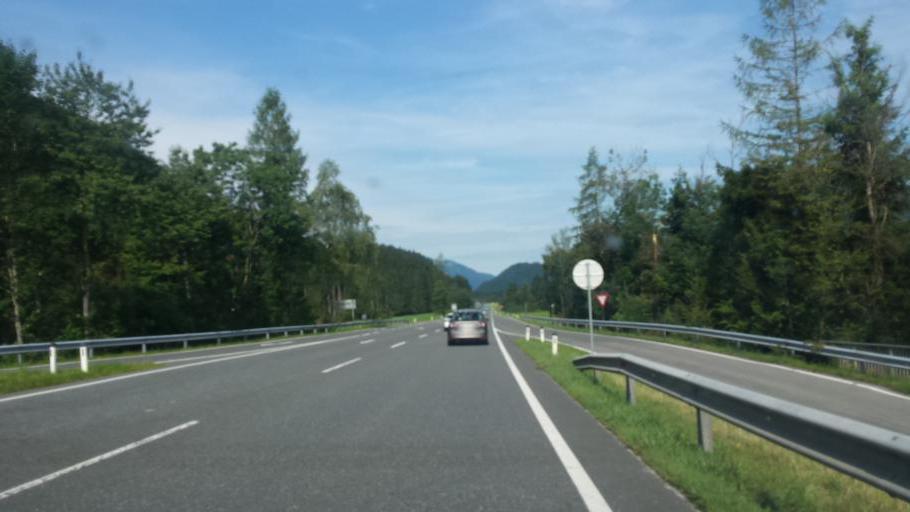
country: AT
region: Salzburg
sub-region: Politischer Bezirk Salzburg-Umgebung
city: Strobl
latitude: 47.7115
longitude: 13.5399
